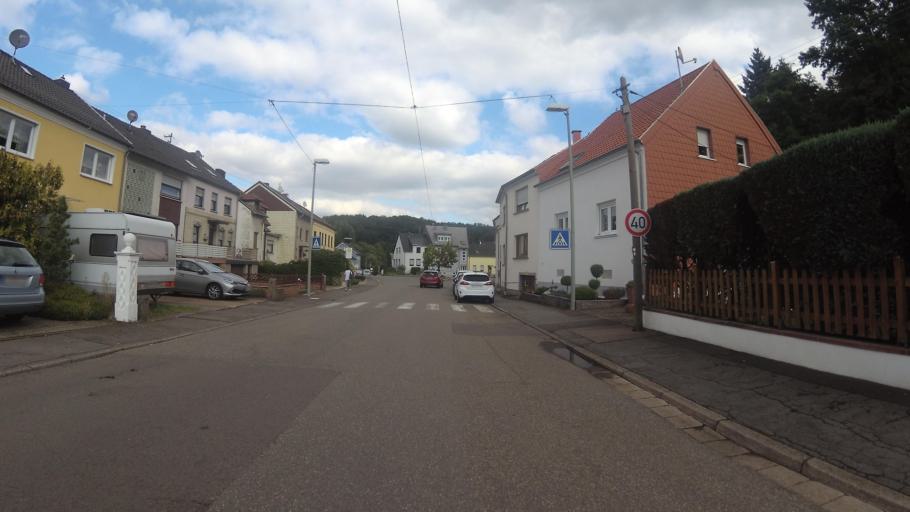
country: DE
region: Saarland
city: Wadgassen
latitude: 49.2427
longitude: 6.7722
